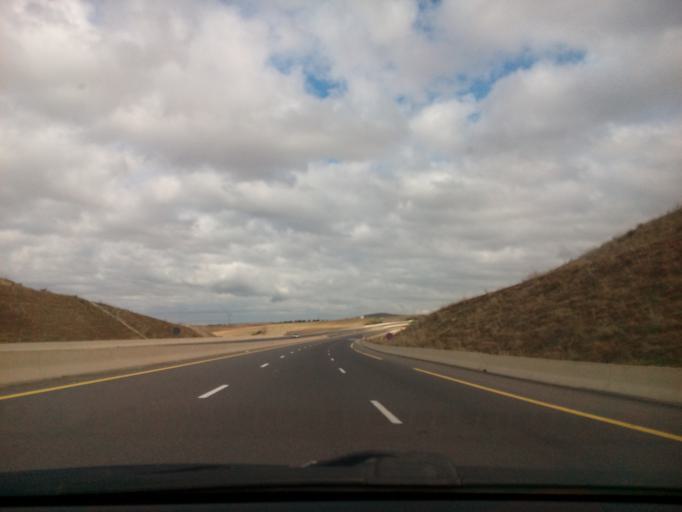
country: DZ
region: Tlemcen
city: Bensekrane
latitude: 35.0065
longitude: -1.1851
